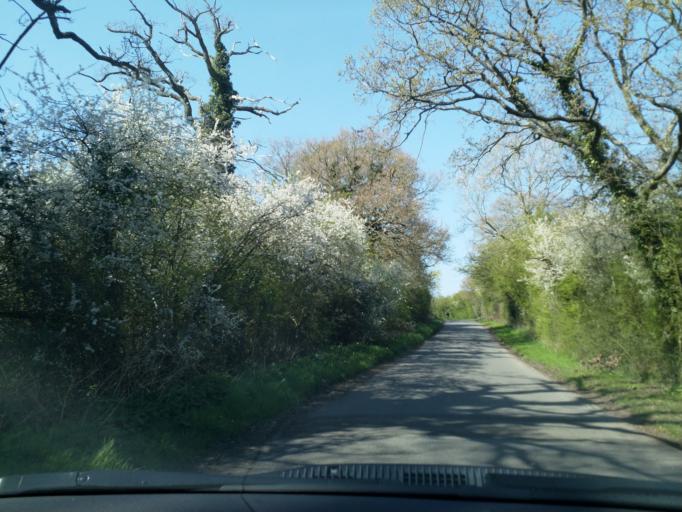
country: GB
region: England
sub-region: Warwickshire
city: Wroxall
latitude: 52.2867
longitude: -1.6708
